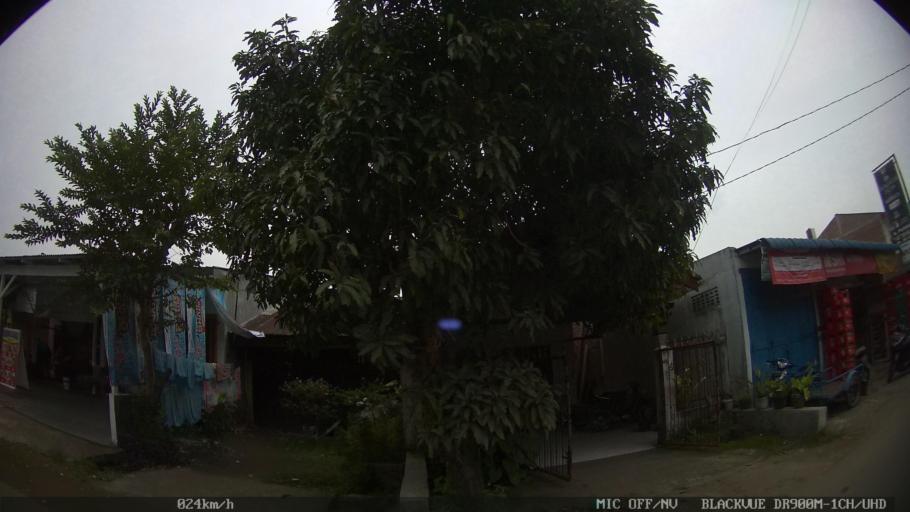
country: ID
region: North Sumatra
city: Deli Tua
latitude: 3.5370
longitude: 98.7324
